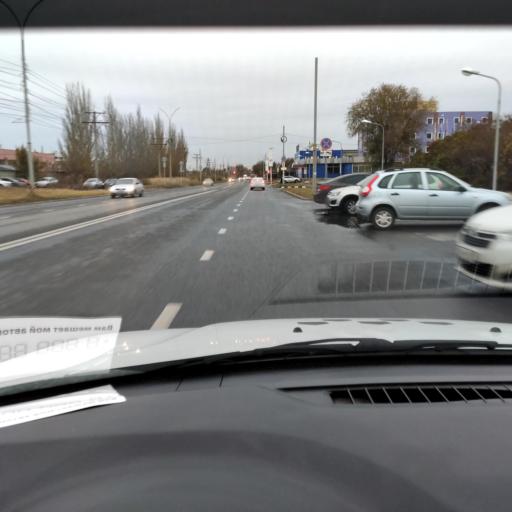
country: RU
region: Samara
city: Tol'yatti
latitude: 53.5580
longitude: 49.2945
